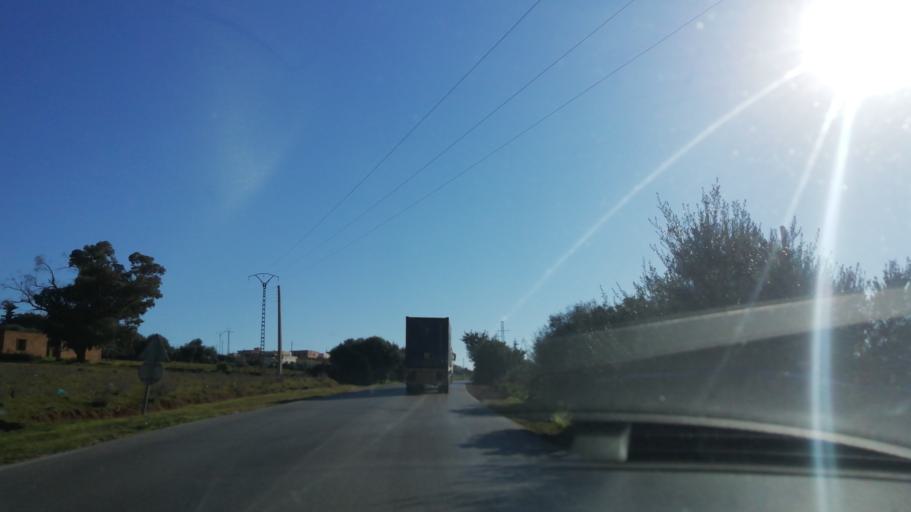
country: DZ
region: Relizane
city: Smala
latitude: 35.6814
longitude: 0.8002
